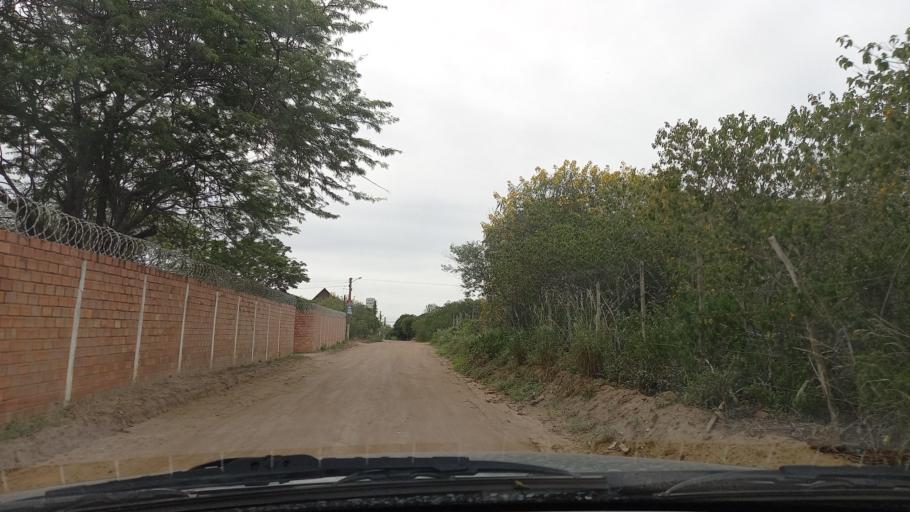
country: BR
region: Pernambuco
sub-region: Gravata
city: Gravata
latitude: -8.1970
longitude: -35.5911
